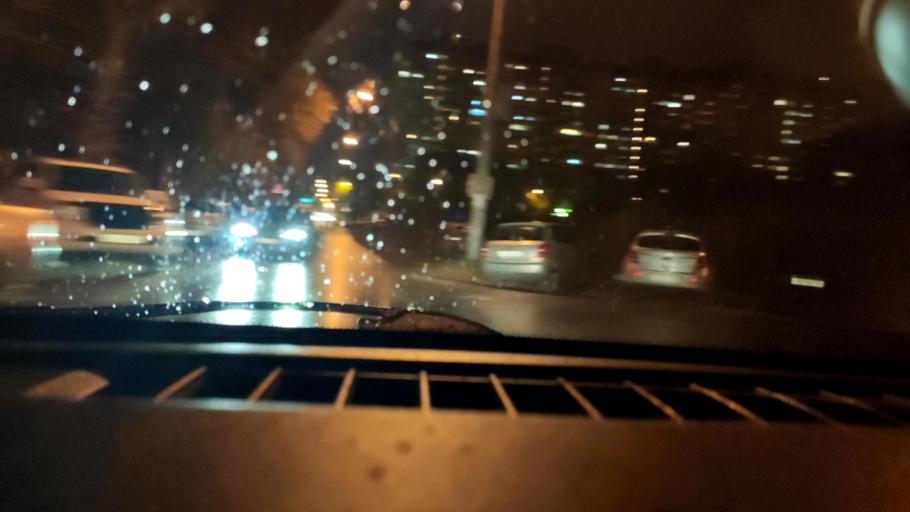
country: RU
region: Samara
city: Samara
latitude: 53.2222
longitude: 50.2453
